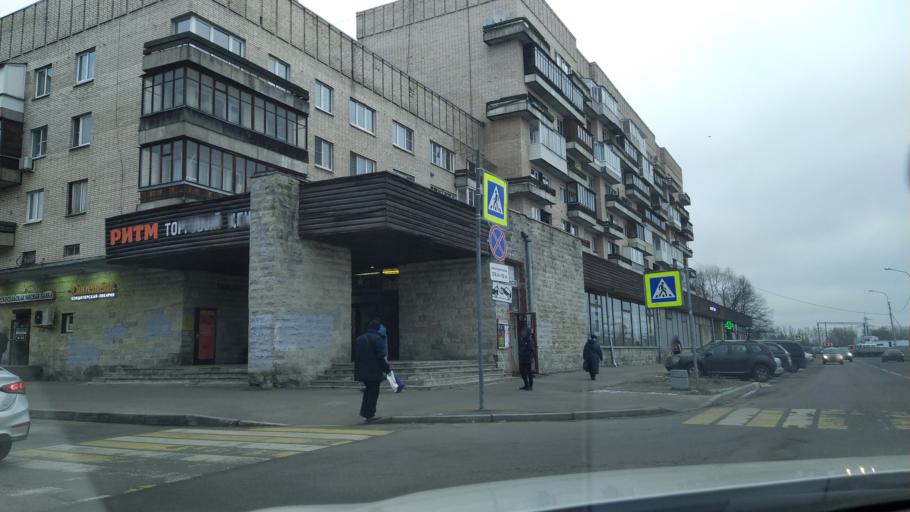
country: RU
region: St.-Petersburg
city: Pushkin
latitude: 59.7301
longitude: 30.4220
